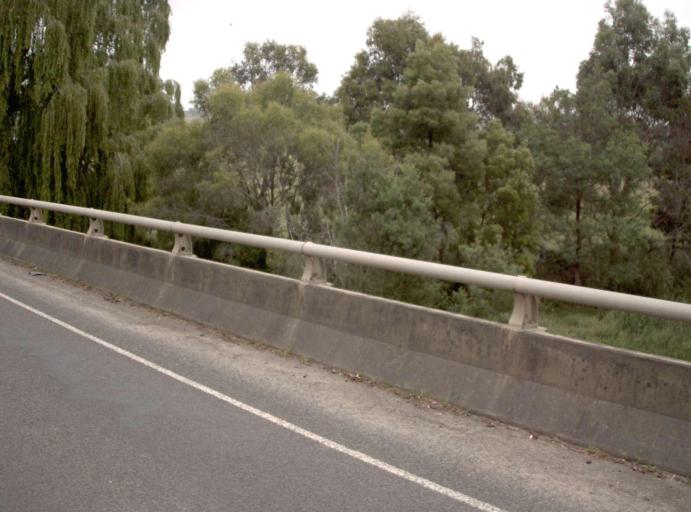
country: AU
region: Victoria
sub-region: Latrobe
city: Traralgon
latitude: -38.2500
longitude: 146.5429
